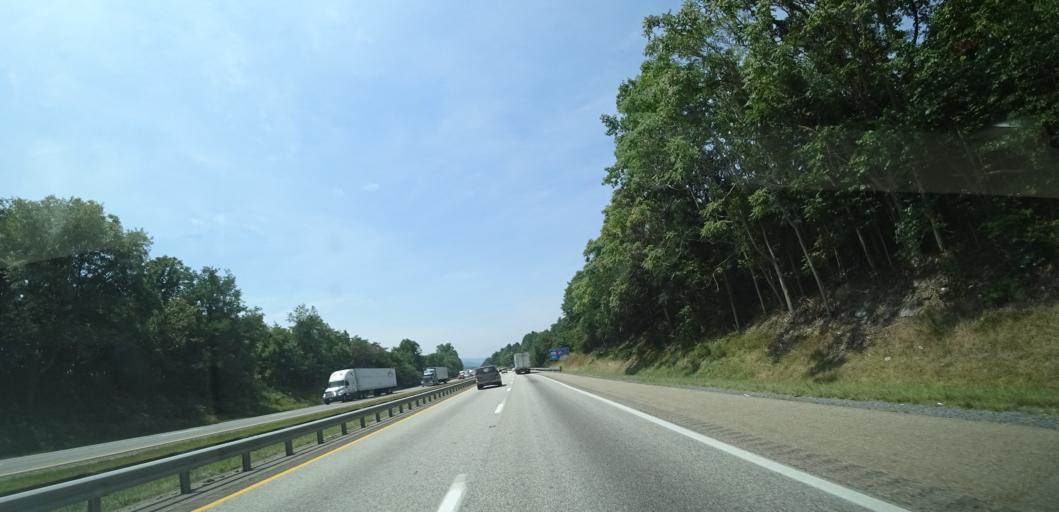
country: US
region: Virginia
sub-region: Botetourt County
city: Buchanan
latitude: 37.5844
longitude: -79.6407
